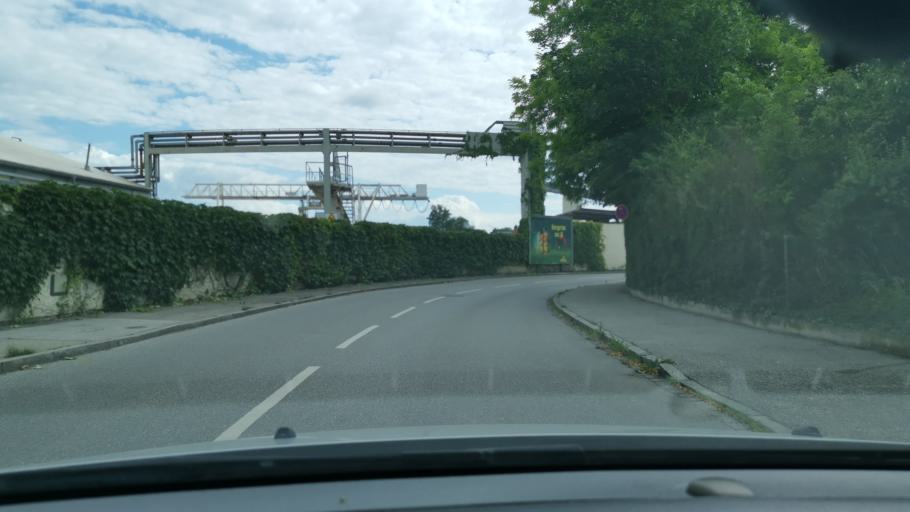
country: DE
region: Bavaria
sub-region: Upper Bavaria
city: Moosburg
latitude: 48.4708
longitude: 11.9408
